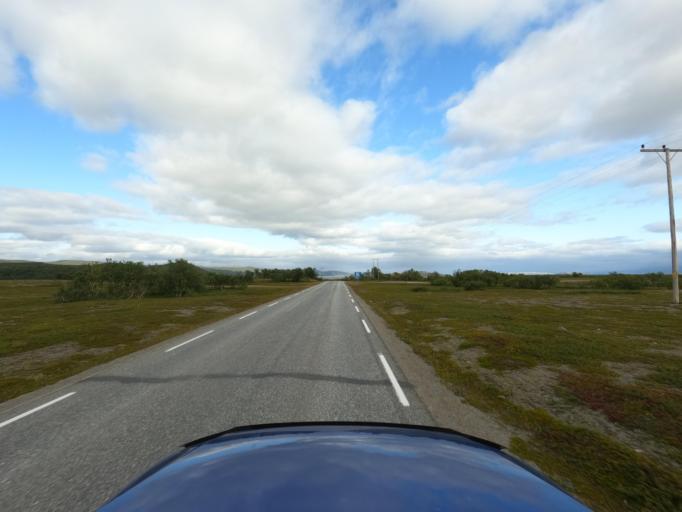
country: NO
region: Finnmark Fylke
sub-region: Porsanger
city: Lakselv
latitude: 70.1676
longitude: 24.9059
